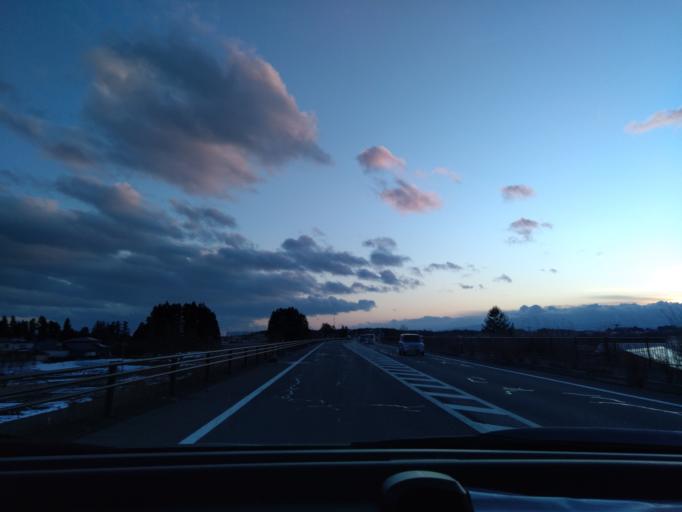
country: JP
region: Iwate
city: Hanamaki
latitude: 39.3746
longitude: 141.1376
